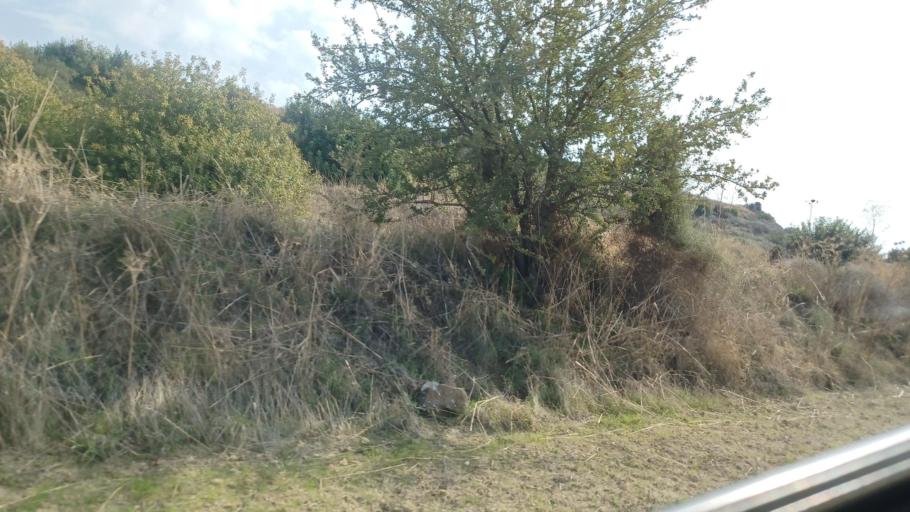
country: CY
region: Pafos
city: Polis
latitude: 34.9741
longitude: 32.4549
